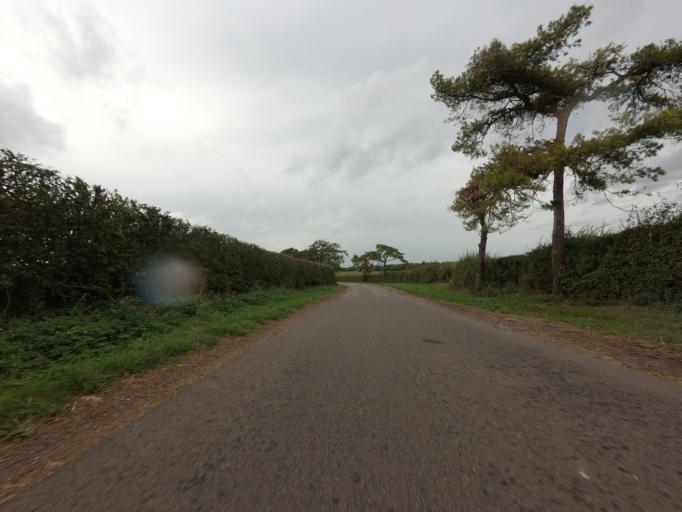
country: GB
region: England
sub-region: Cambridgeshire
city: Duxford
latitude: 52.0610
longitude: 0.1160
